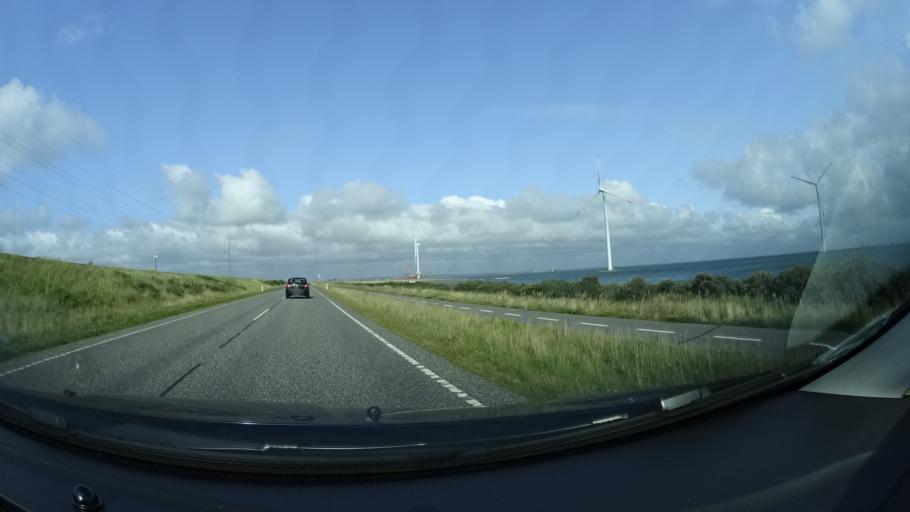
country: DK
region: Central Jutland
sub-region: Lemvig Kommune
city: Thyboron
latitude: 56.6695
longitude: 8.2090
